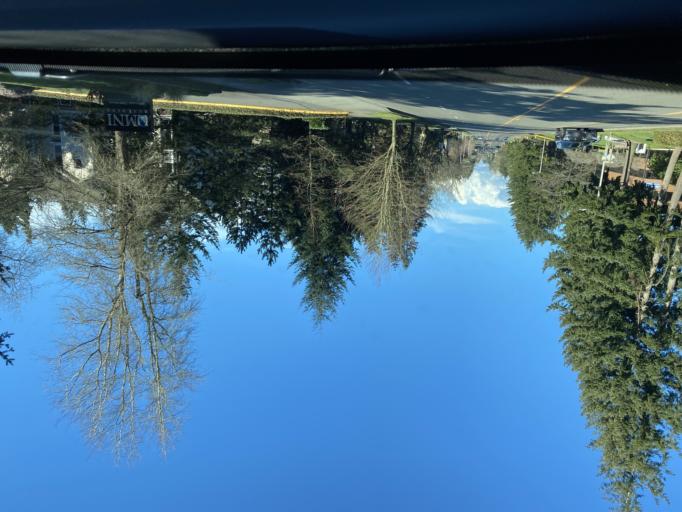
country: US
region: Washington
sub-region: King County
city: Federal Way
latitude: 47.3007
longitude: -122.3219
